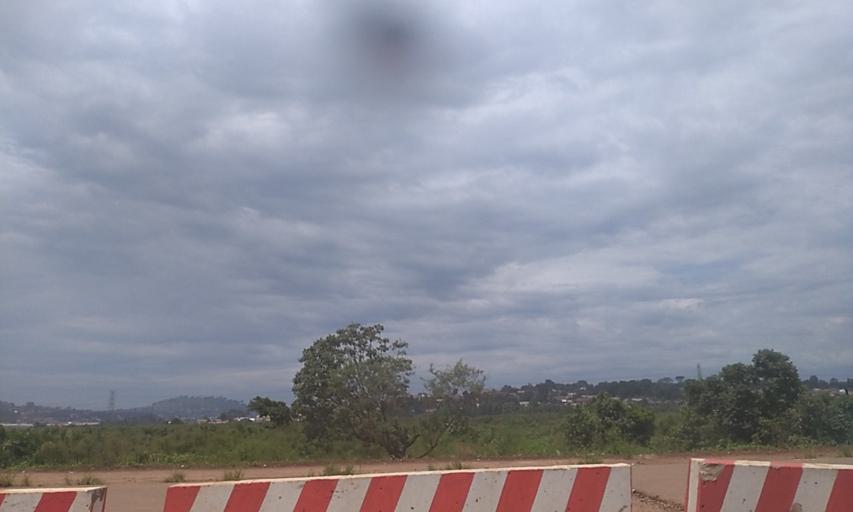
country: UG
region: Central Region
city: Kampala Central Division
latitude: 0.3352
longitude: 32.5293
